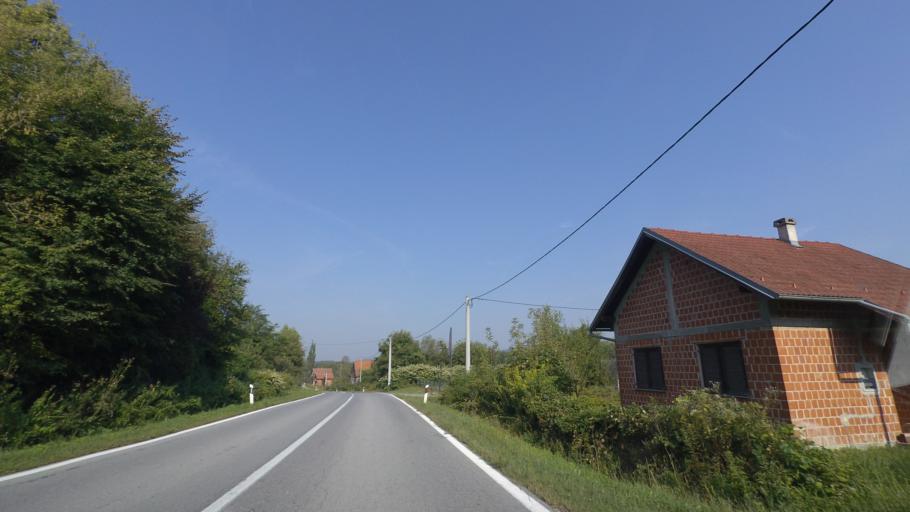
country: HR
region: Bjelovarsko-Bilogorska
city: Sirac
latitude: 45.4668
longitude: 17.3931
